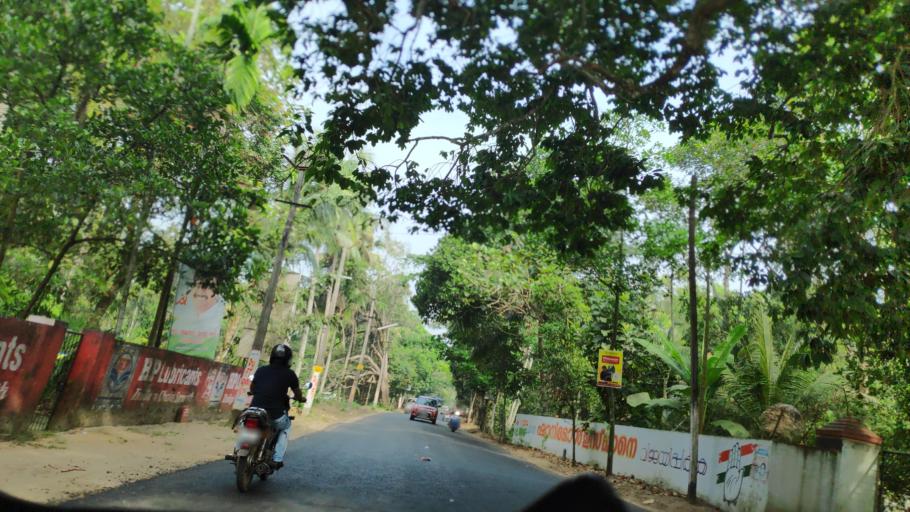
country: IN
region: Kerala
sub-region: Alappuzha
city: Kutiatodu
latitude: 9.7746
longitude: 76.3614
